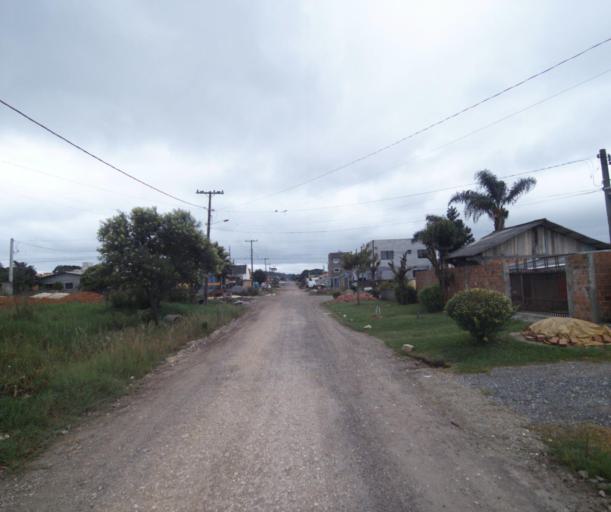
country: BR
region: Parana
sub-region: Quatro Barras
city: Quatro Barras
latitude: -25.3648
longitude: -49.0927
